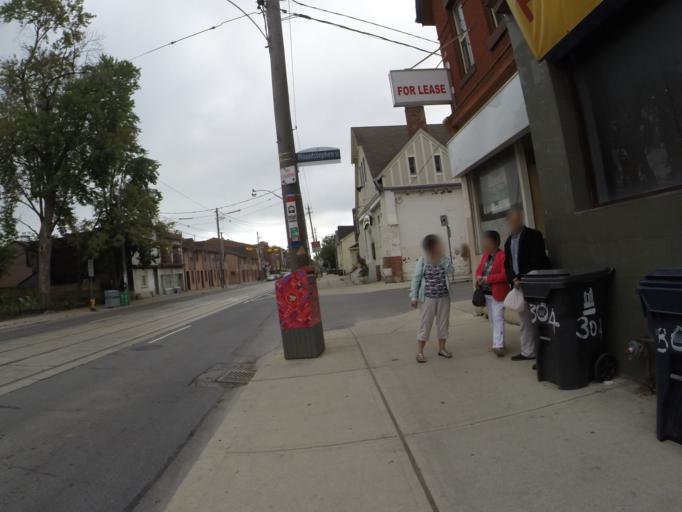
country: CA
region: Ontario
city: Toronto
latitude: 43.6653
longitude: -79.3527
